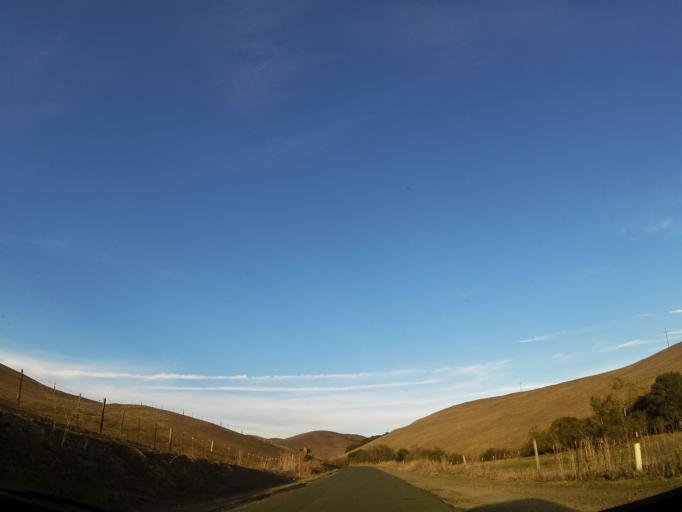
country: US
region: California
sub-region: San Benito County
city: San Juan Bautista
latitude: 36.7931
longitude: -121.5833
